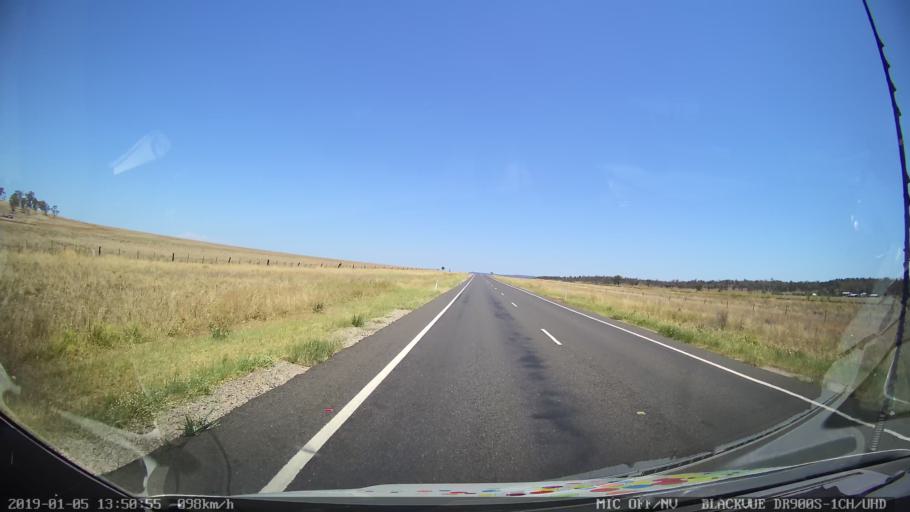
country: AU
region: New South Wales
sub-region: Gunnedah
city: Gunnedah
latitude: -31.0368
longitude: 150.2758
